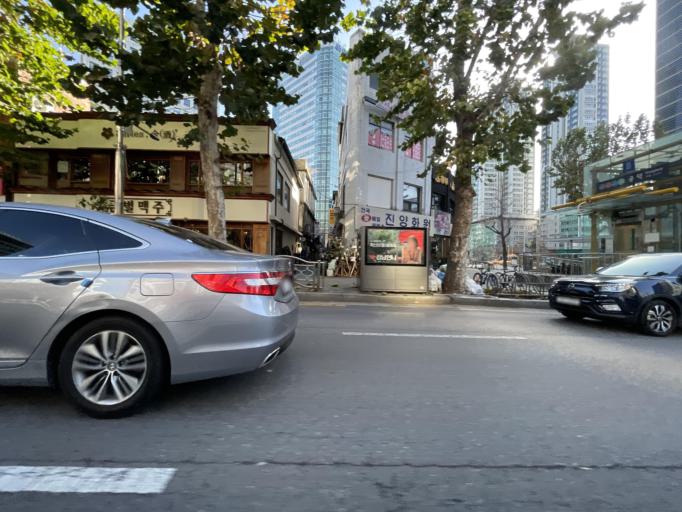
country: KR
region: Seoul
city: Seoul
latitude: 37.5445
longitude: 126.9515
